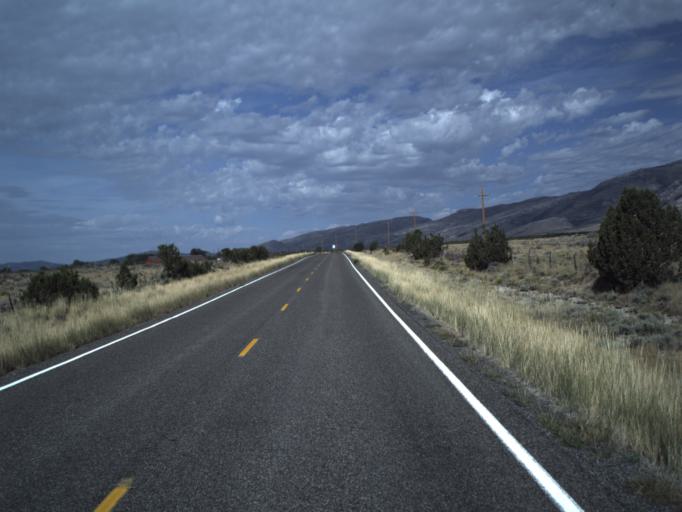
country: US
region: Idaho
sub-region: Cassia County
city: Burley
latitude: 41.8176
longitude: -113.3945
